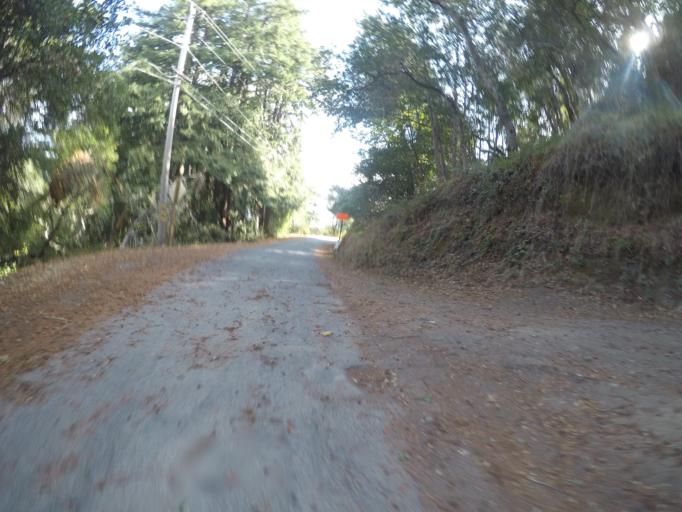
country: US
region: California
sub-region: Santa Cruz County
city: Scotts Valley
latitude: 37.0441
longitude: -121.9652
